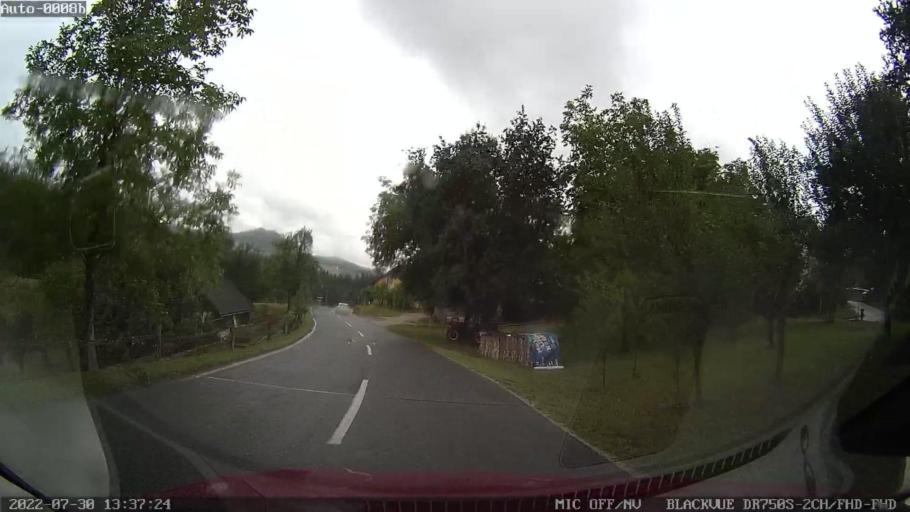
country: SI
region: Zuzemberk
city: Zuzemberk
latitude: 45.8763
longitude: 14.9177
